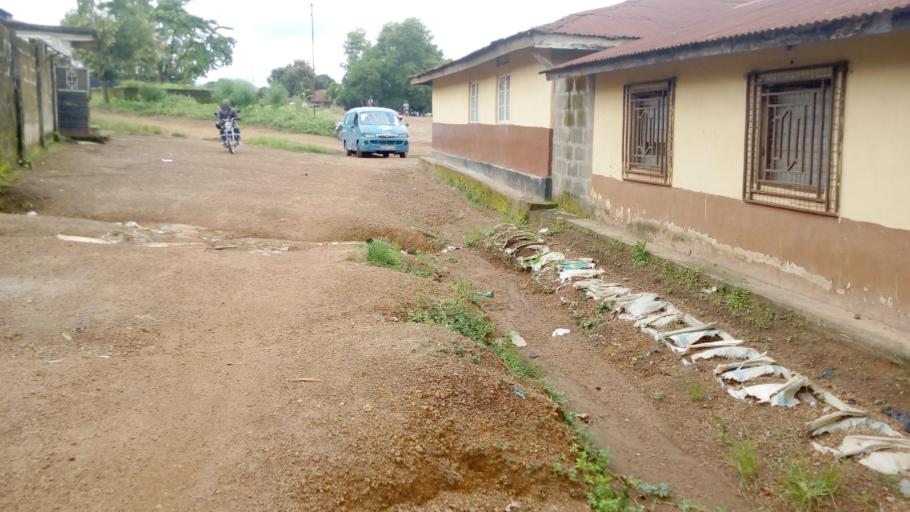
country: SL
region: Northern Province
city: Makeni
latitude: 8.8889
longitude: -12.0299
